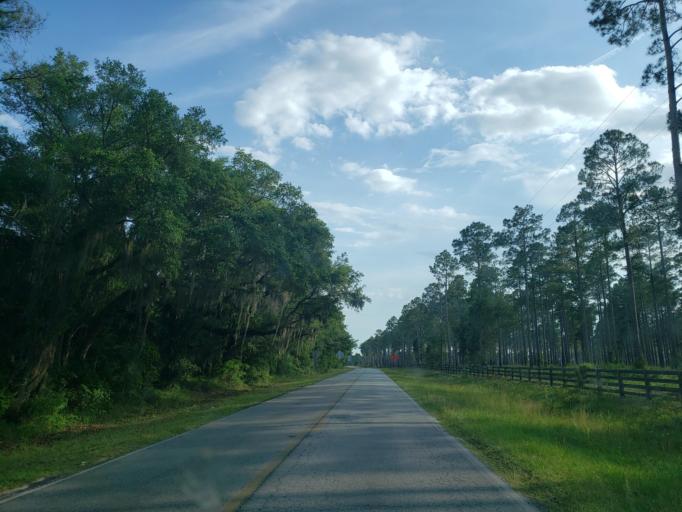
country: US
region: Georgia
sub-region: Echols County
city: Statenville
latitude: 30.6385
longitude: -83.1943
